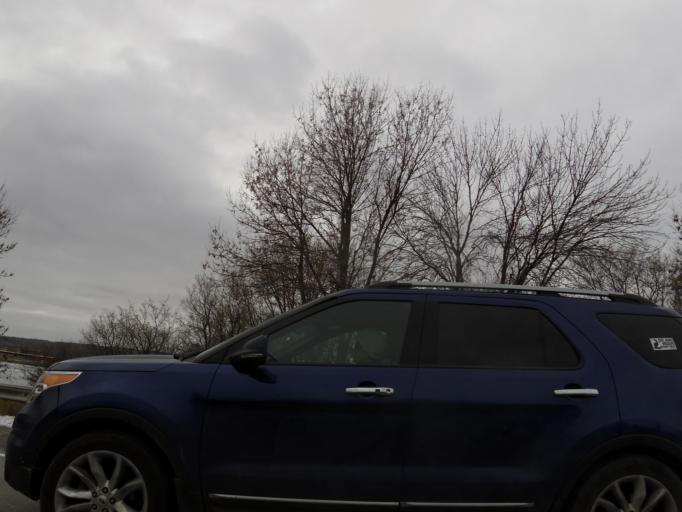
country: US
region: Minnesota
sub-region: Ramsey County
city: Maplewood
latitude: 44.9422
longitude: -93.0344
